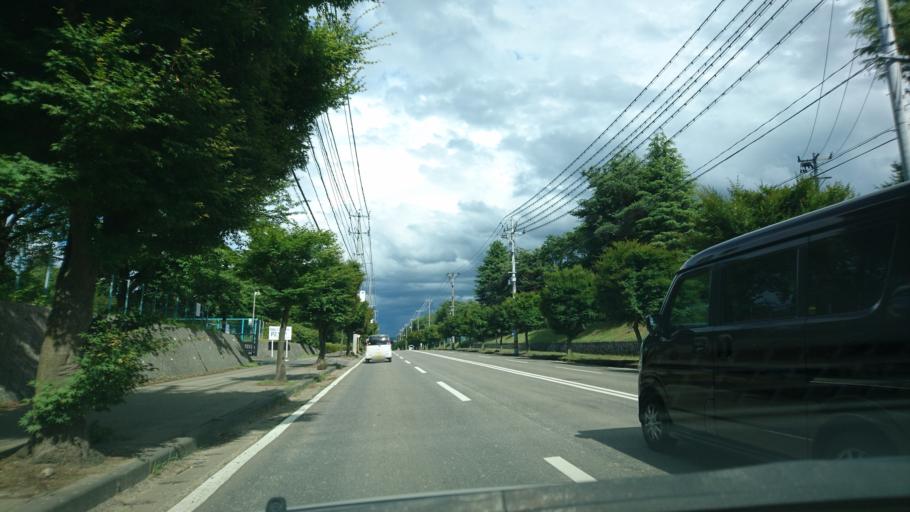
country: JP
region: Iwate
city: Hanamaki
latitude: 39.3351
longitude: 141.1240
